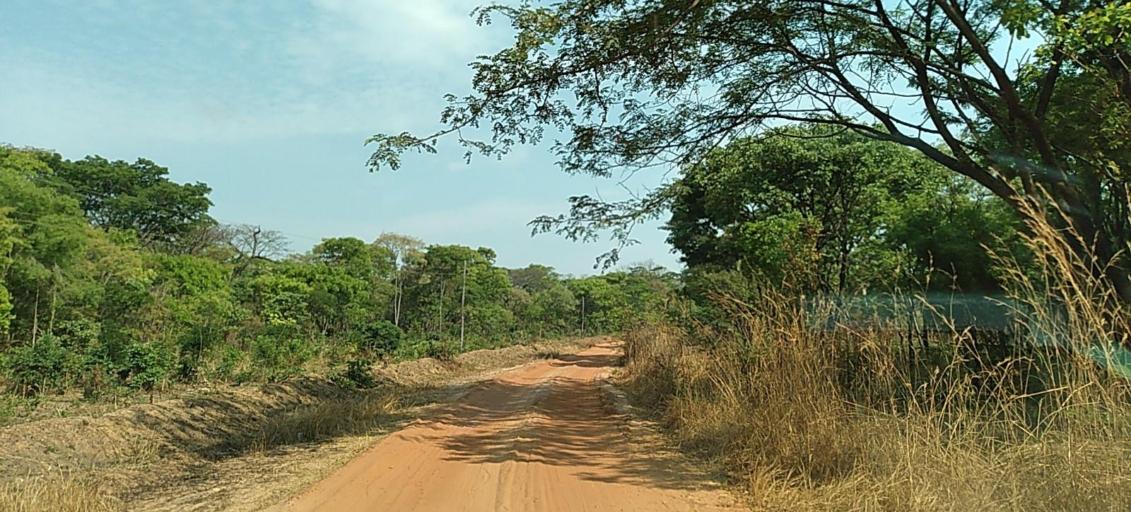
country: ZM
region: Copperbelt
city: Kalulushi
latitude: -13.0090
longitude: 27.8138
